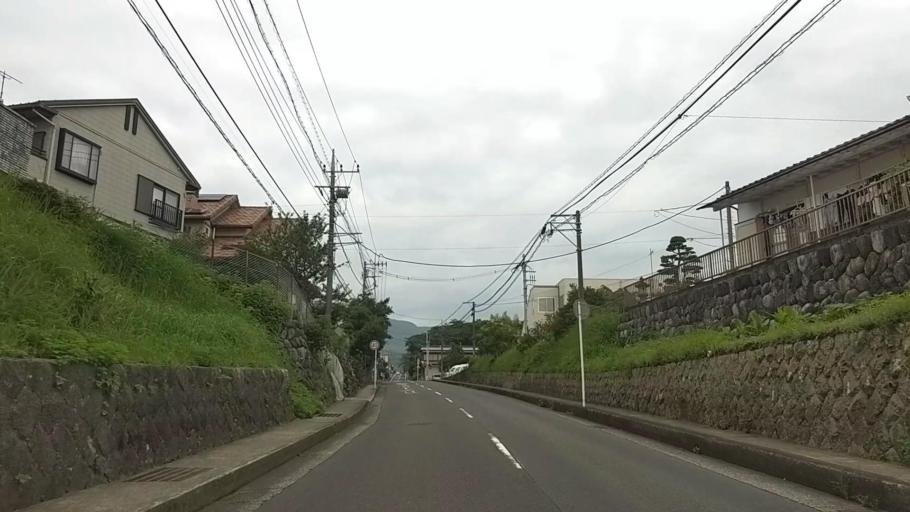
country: JP
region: Kanagawa
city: Odawara
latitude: 35.3256
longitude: 139.0936
